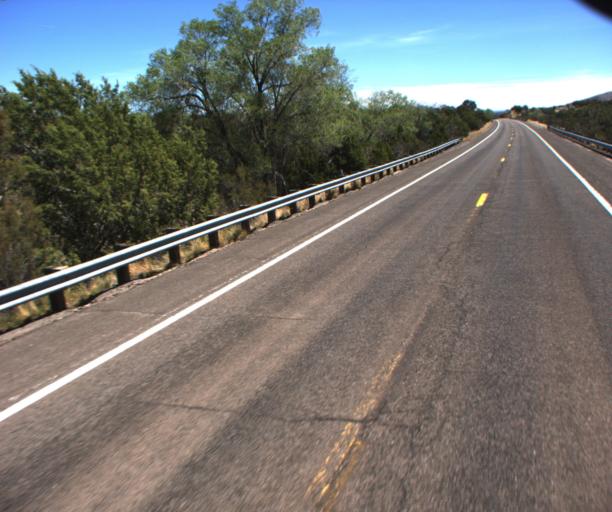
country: US
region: Arizona
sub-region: Mohave County
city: Peach Springs
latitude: 35.5531
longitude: -113.3674
